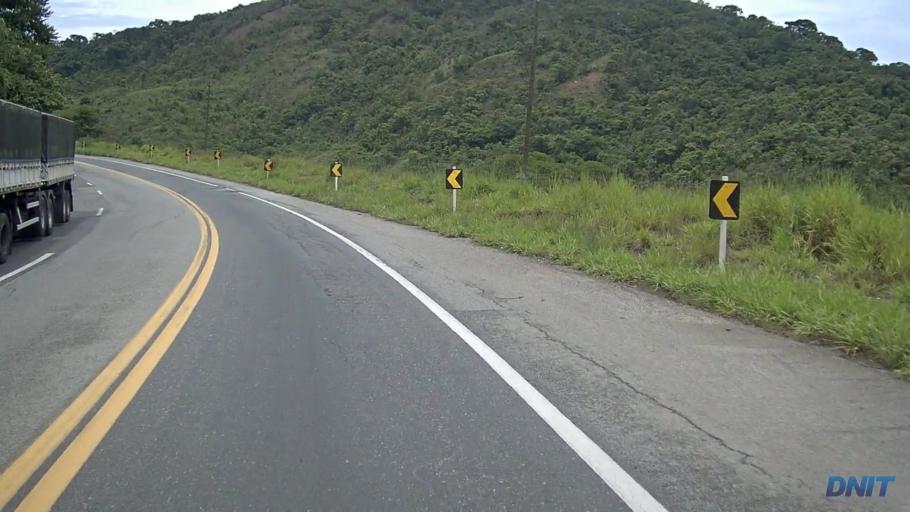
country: BR
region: Minas Gerais
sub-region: Nova Era
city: Nova Era
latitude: -19.6336
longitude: -42.8922
